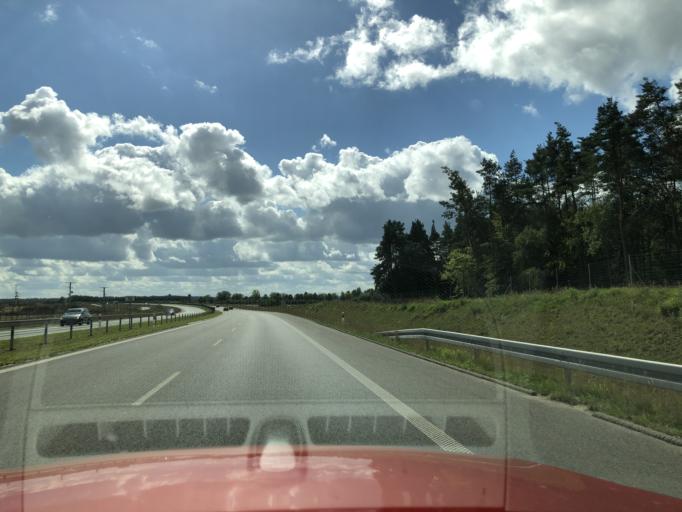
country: PL
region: West Pomeranian Voivodeship
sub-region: Powiat szczecinecki
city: Szczecinek
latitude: 53.6619
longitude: 16.7374
